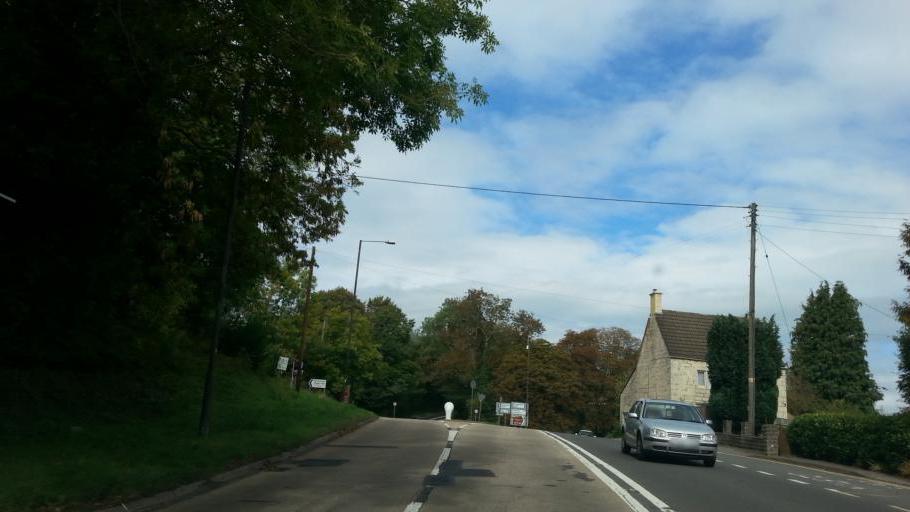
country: GB
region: England
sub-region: Gloucestershire
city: Stroud
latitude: 51.7680
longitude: -2.2180
